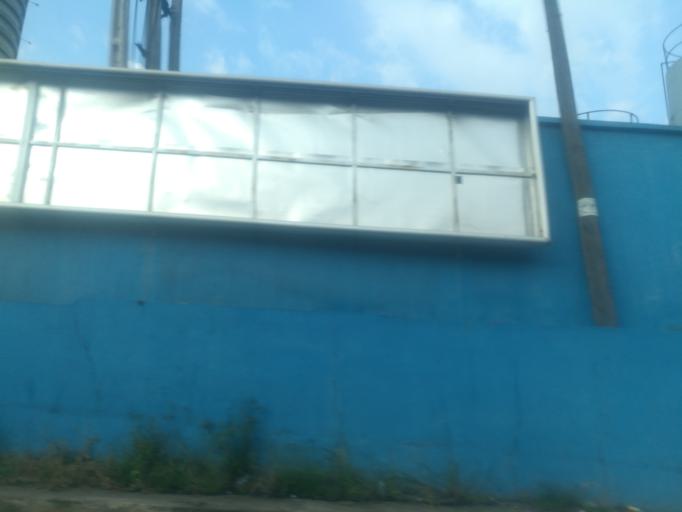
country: NG
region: Oyo
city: Ibadan
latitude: 7.3867
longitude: 3.8793
